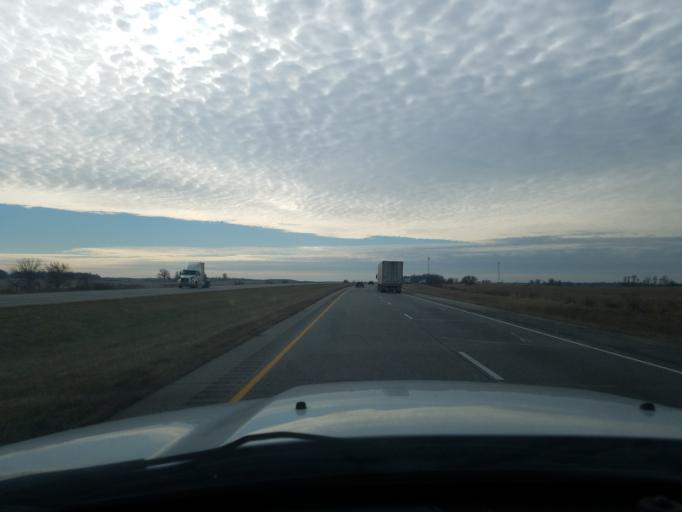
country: US
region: Indiana
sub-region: Huntington County
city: Warren
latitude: 40.7381
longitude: -85.4149
